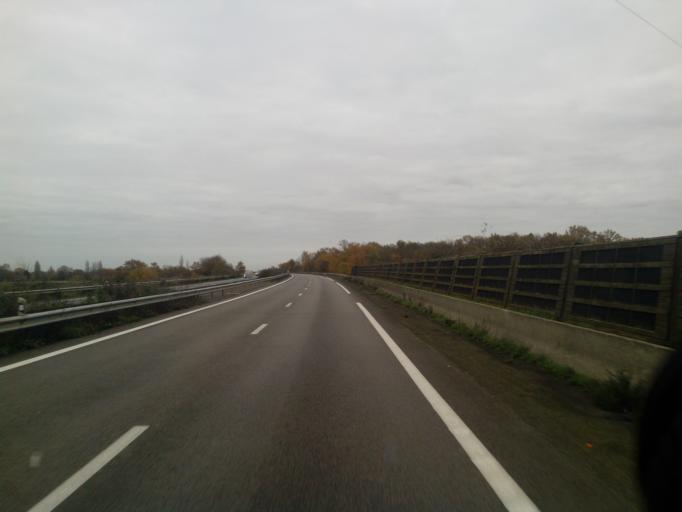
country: FR
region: Pays de la Loire
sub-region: Departement de la Loire-Atlantique
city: La Chapelle-Heulin
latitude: 47.1579
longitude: -1.3389
